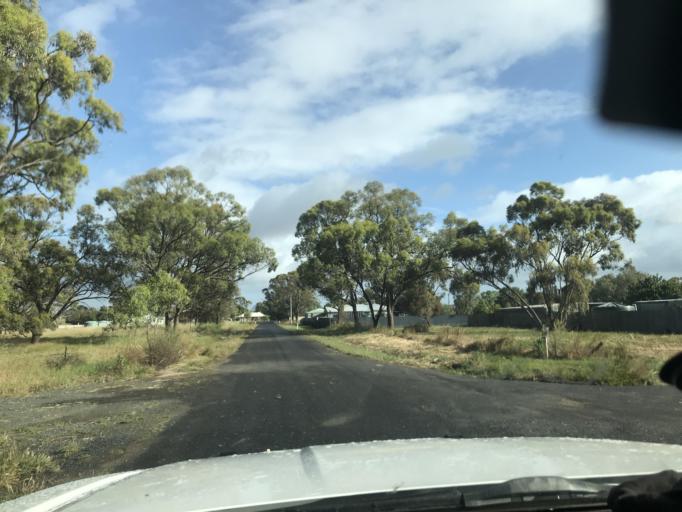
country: AU
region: Victoria
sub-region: Horsham
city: Horsham
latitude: -36.7218
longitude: 141.4711
